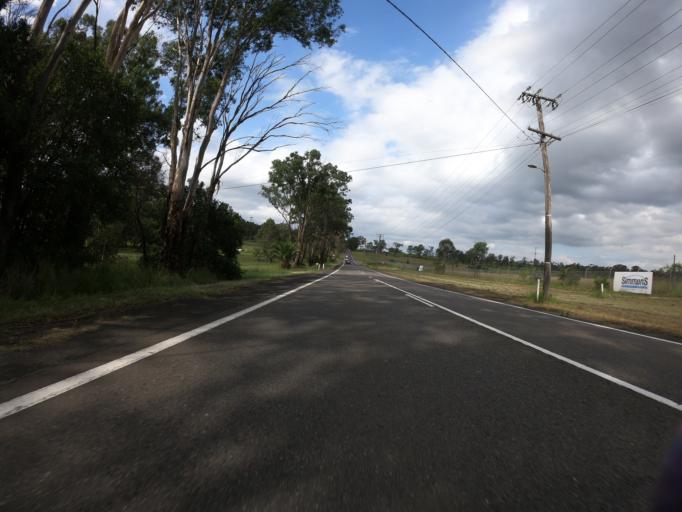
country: AU
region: New South Wales
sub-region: Blacktown
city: Riverstone
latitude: -33.6677
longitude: 150.8837
